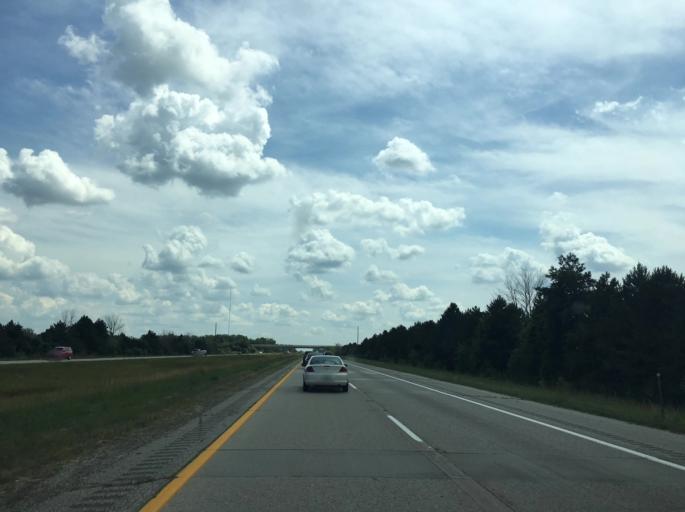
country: US
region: Michigan
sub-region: Bay County
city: Auburn
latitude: 43.7151
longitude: -84.0124
